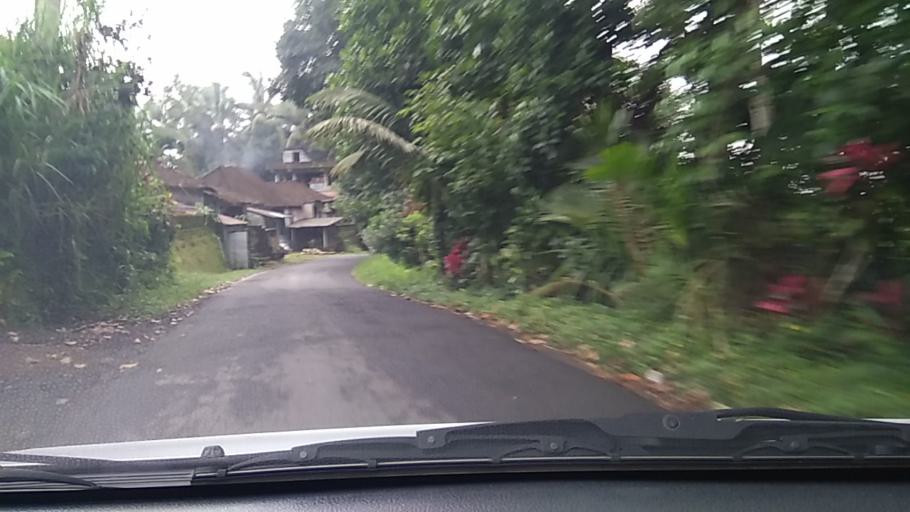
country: ID
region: Bali
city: Tegalalang
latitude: -8.4200
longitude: 115.2807
